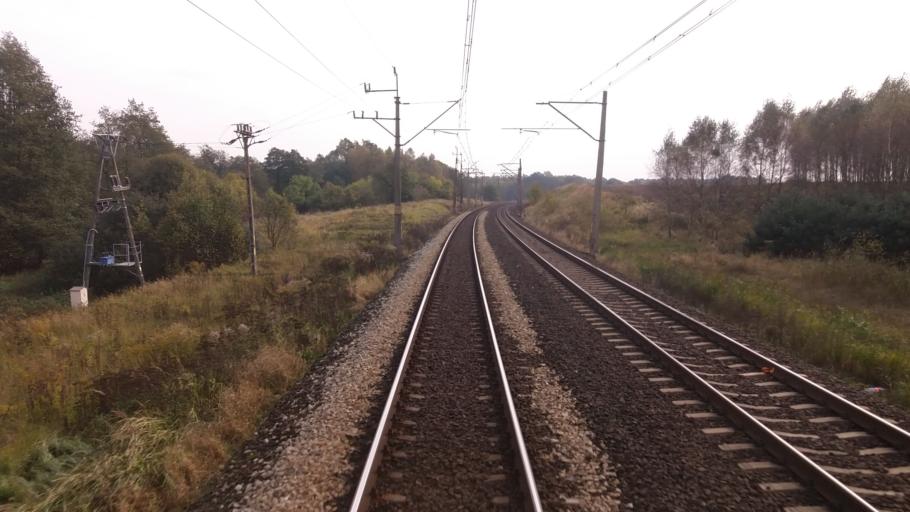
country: PL
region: West Pomeranian Voivodeship
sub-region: Powiat stargardzki
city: Dolice
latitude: 53.1804
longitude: 15.2763
